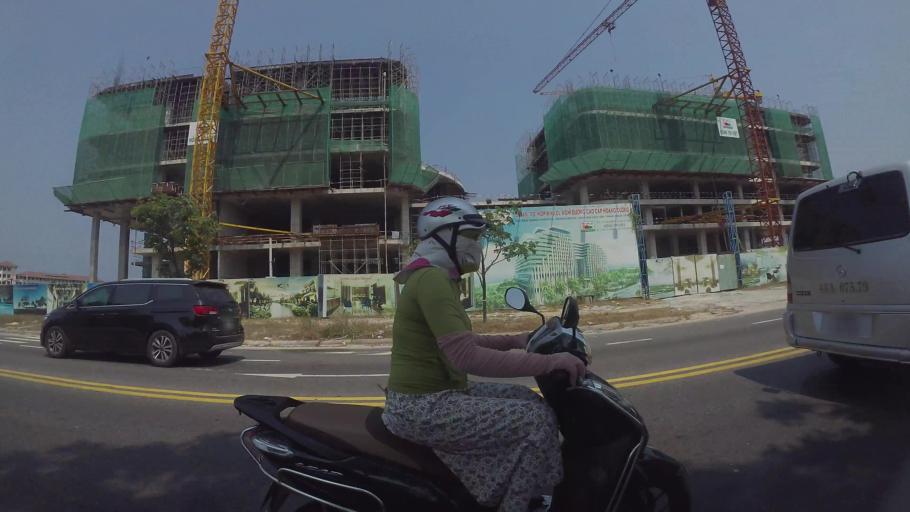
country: VN
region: Da Nang
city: Ngu Hanh Son
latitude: 16.0036
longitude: 108.2665
